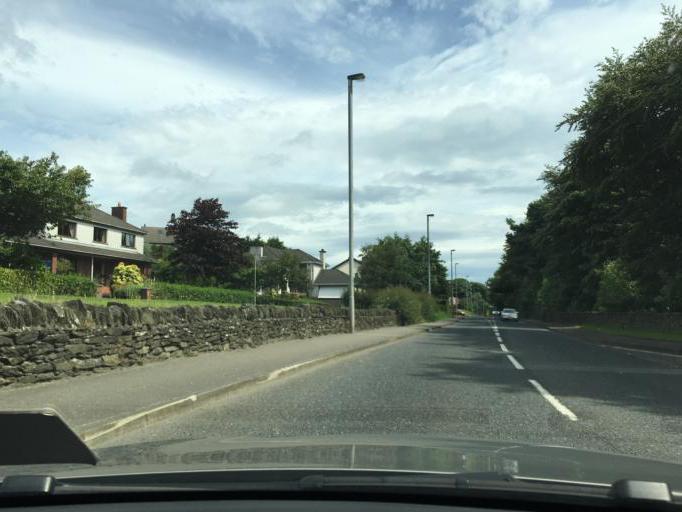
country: GB
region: Northern Ireland
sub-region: City of Derry
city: Derry
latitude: 55.0302
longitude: -7.2963
